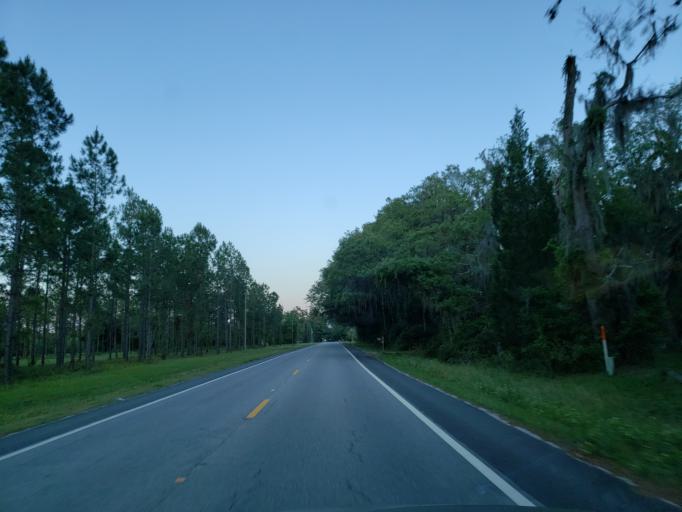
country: US
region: Florida
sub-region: Hamilton County
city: Jasper
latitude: 30.5534
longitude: -83.0689
